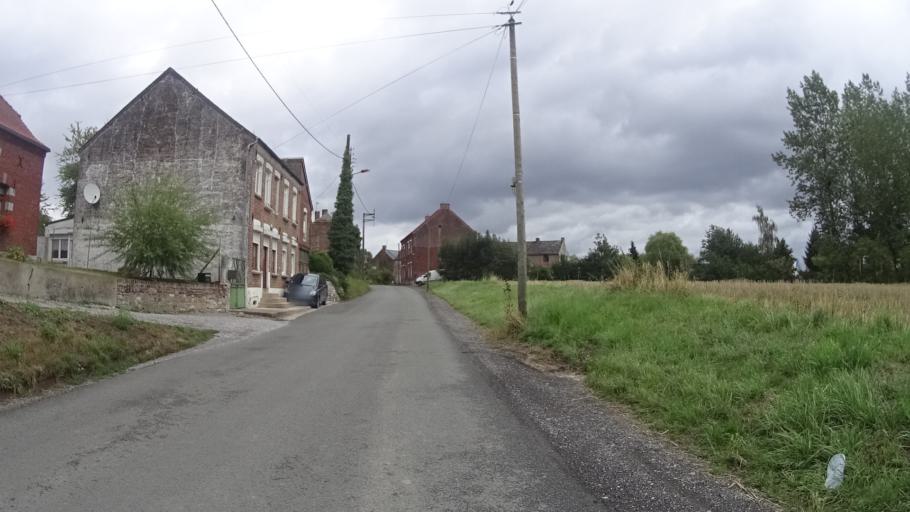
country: FR
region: Nord-Pas-de-Calais
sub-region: Departement du Nord
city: Berlaimont
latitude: 50.1780
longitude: 3.8035
